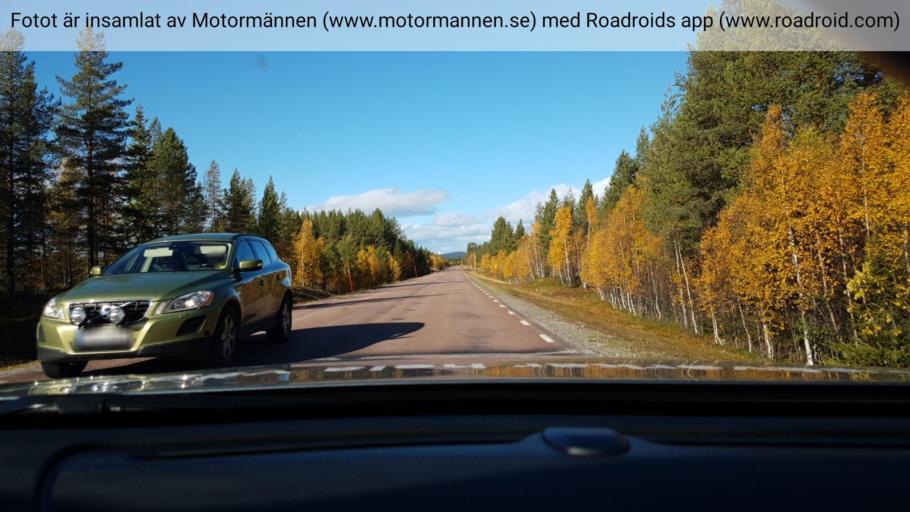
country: SE
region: Norrbotten
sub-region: Arjeplogs Kommun
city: Arjeplog
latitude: 66.0046
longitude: 18.1128
